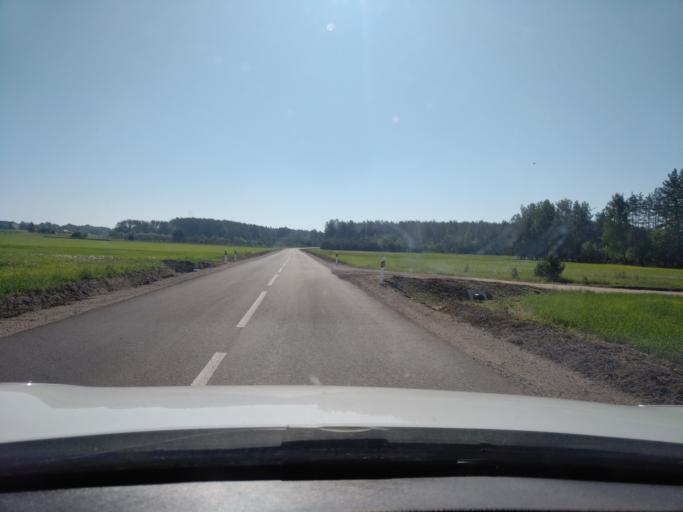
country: LT
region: Utenos apskritis
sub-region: Utena
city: Utena
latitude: 55.6639
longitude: 25.4616
